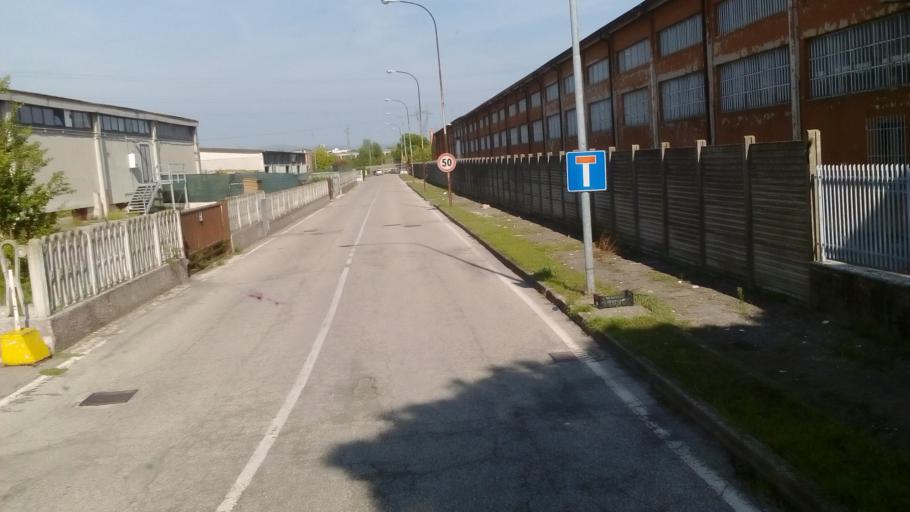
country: IT
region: Veneto
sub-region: Provincia di Verona
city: San Giovanni Lupatoto
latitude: 45.3882
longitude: 11.0198
